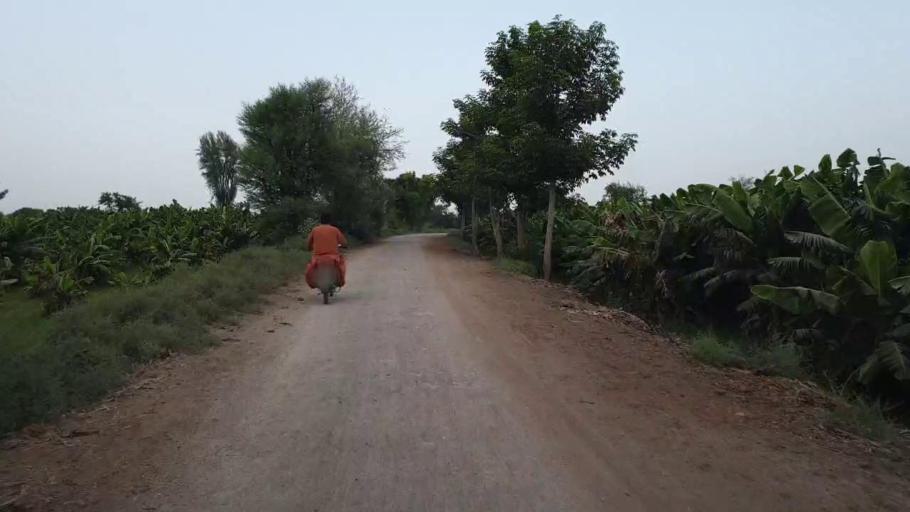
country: PK
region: Sindh
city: Bandhi
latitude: 26.5334
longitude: 68.2034
